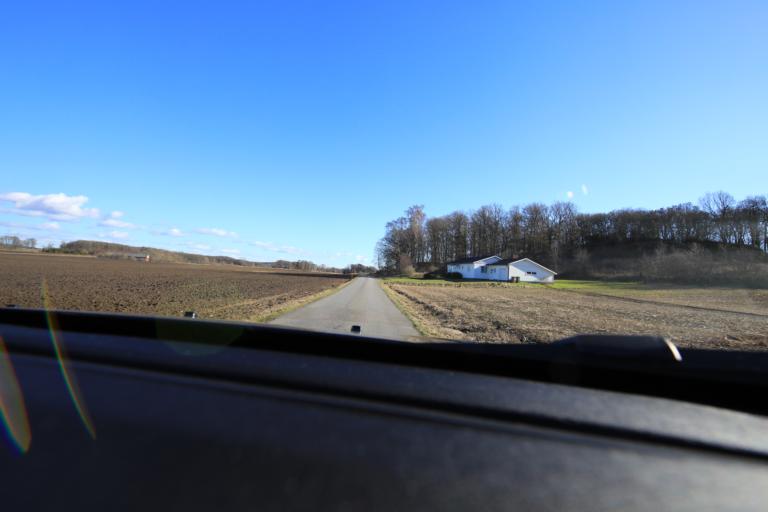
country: SE
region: Halland
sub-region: Varbergs Kommun
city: Tvaaker
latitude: 57.0615
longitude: 12.3719
